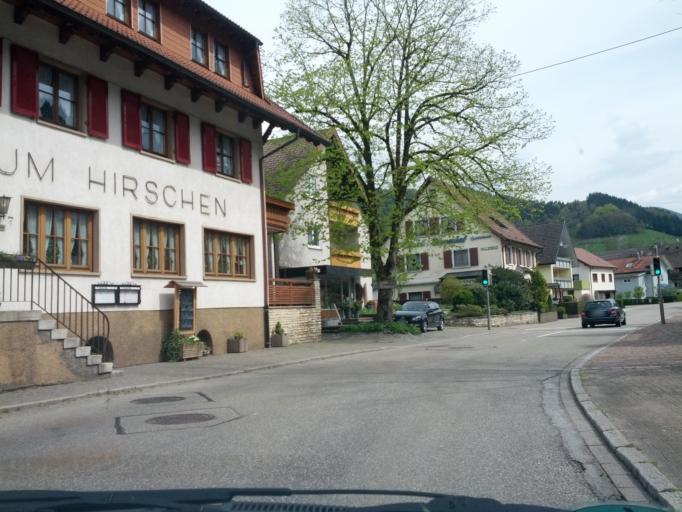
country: DE
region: Baden-Wuerttemberg
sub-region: Freiburg Region
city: Elzach
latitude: 48.1003
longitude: 8.0564
